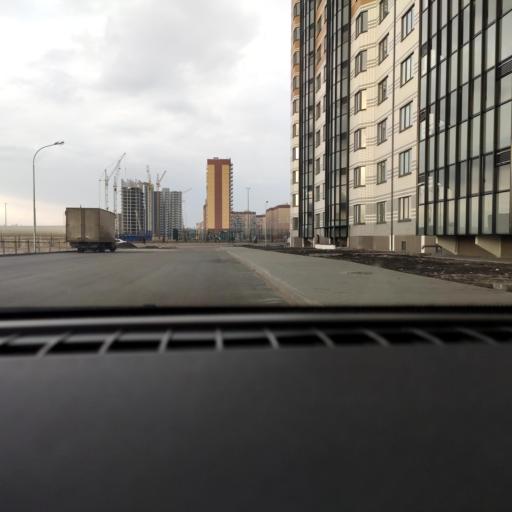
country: RU
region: Voronezj
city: Voronezh
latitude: 51.7127
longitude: 39.2637
